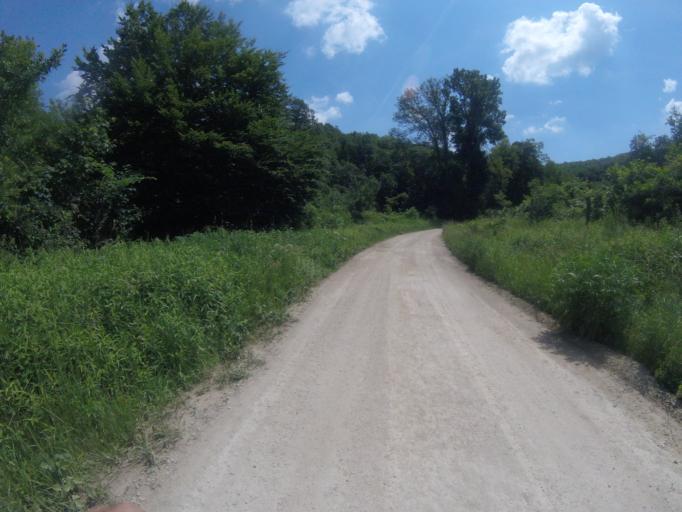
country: HU
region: Veszprem
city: Cseteny
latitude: 47.2661
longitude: 17.9993
